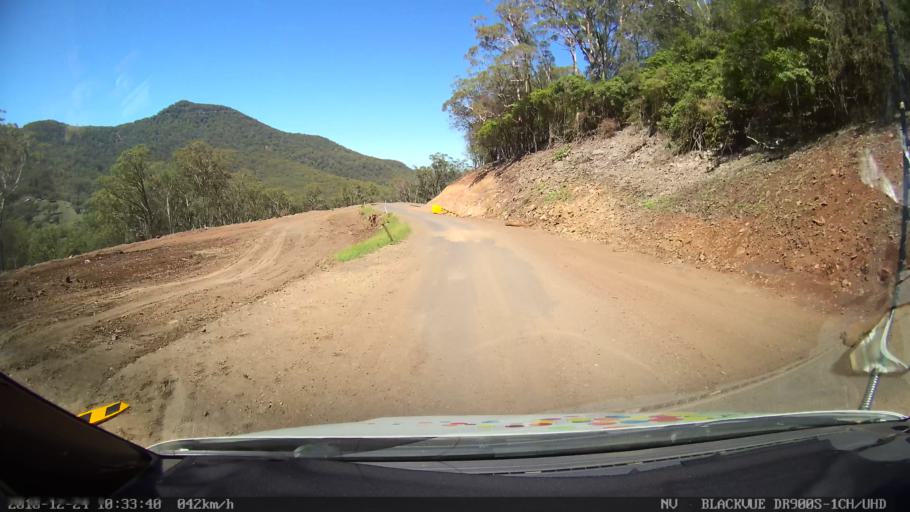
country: AU
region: New South Wales
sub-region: Upper Hunter Shire
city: Merriwa
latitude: -31.8427
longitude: 150.5095
